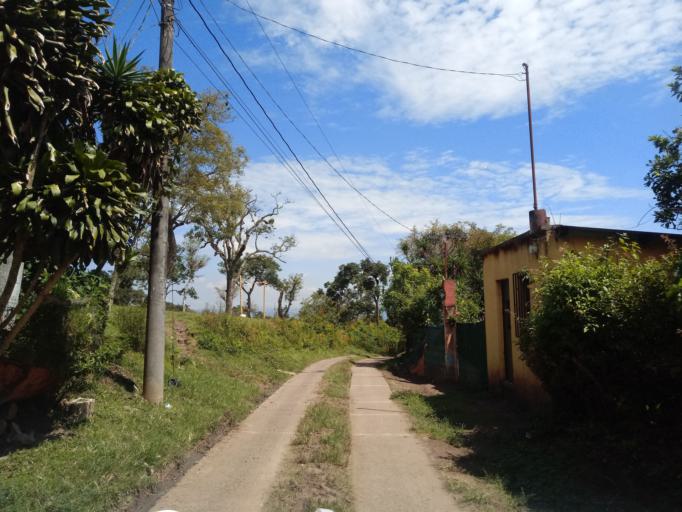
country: GT
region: Guatemala
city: Amatitlan
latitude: 14.4604
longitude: -90.6072
